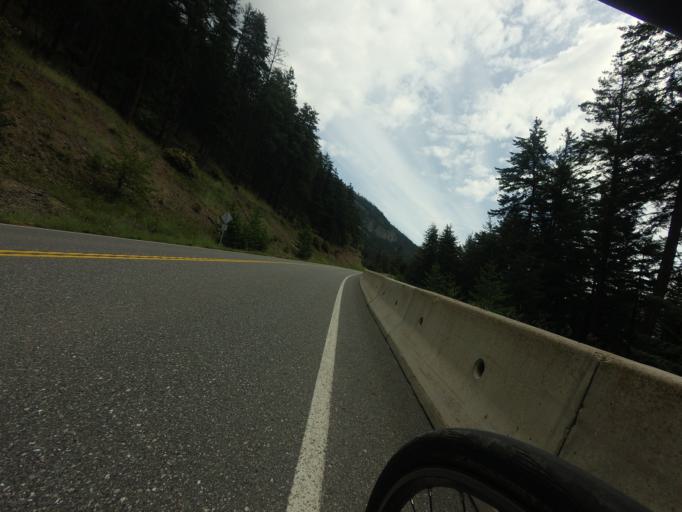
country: CA
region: British Columbia
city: Lillooet
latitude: 50.6446
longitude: -122.0232
